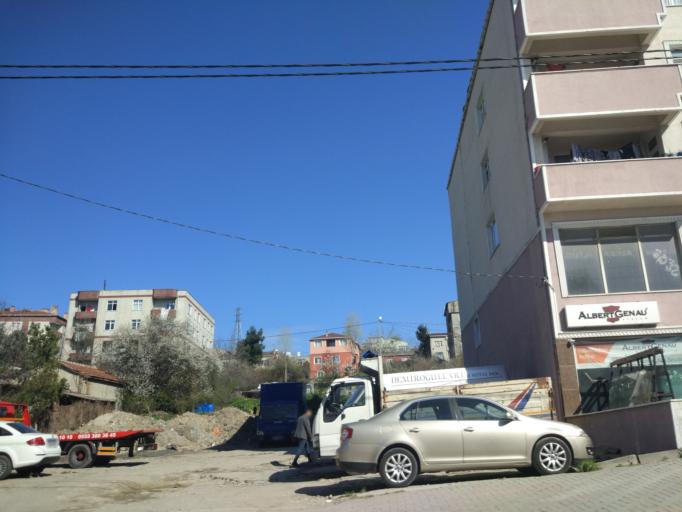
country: TR
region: Istanbul
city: Basaksehir
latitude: 41.0596
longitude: 28.7490
